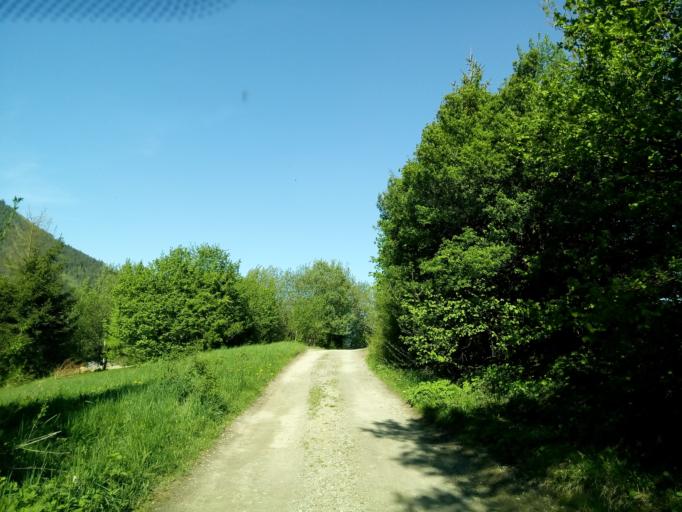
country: SK
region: Zilinsky
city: Ruzomberok
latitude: 49.0818
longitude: 19.2750
